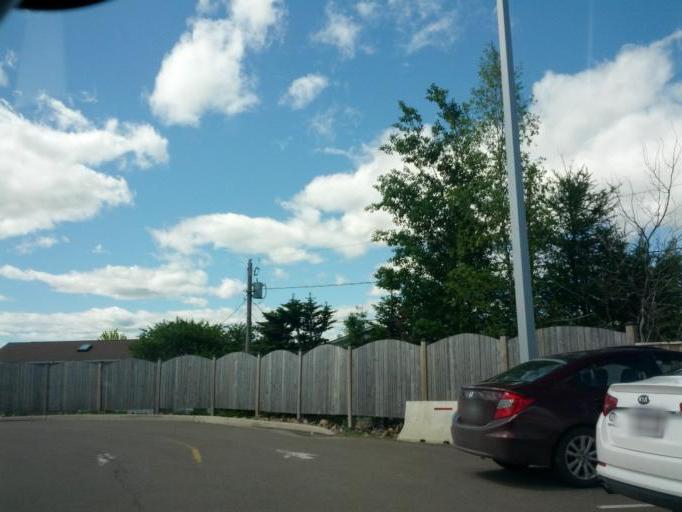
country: CA
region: New Brunswick
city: Moncton
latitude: 46.1236
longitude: -64.8540
